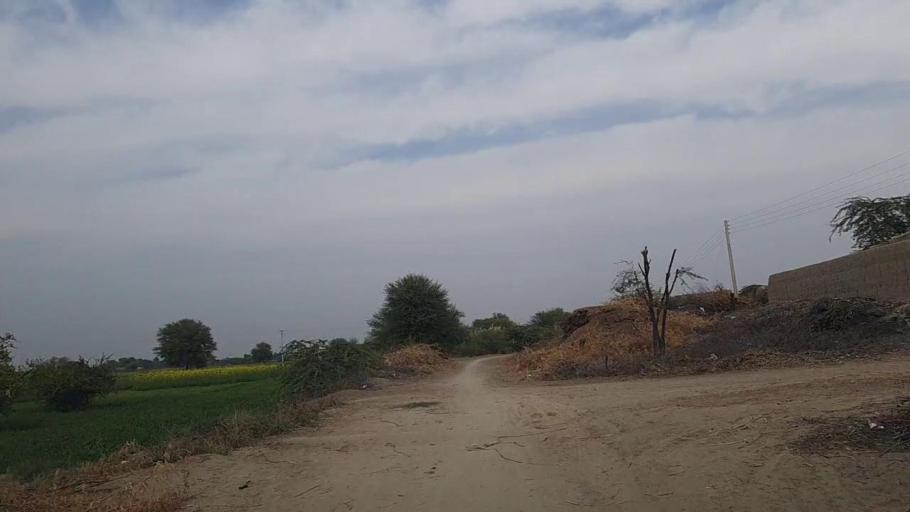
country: PK
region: Sindh
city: Daur
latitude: 26.4362
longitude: 68.4701
